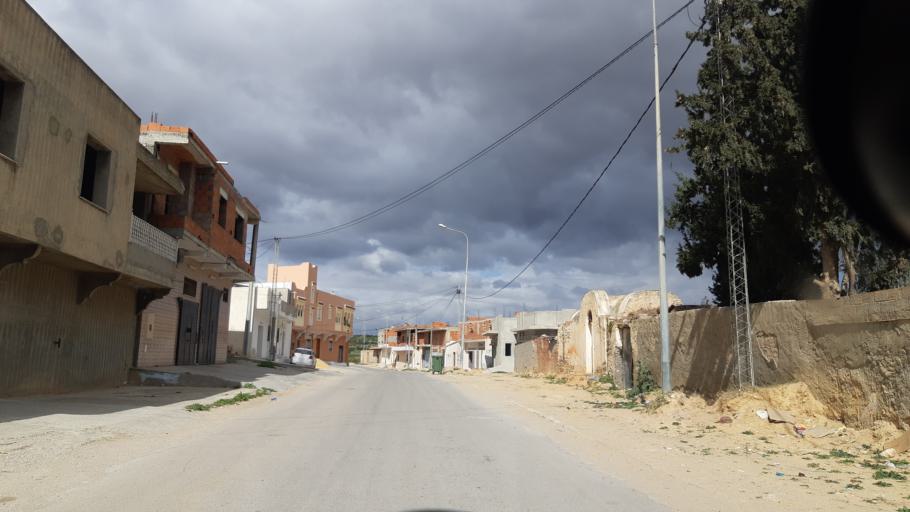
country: TN
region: Susah
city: Akouda
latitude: 35.8727
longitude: 10.5206
